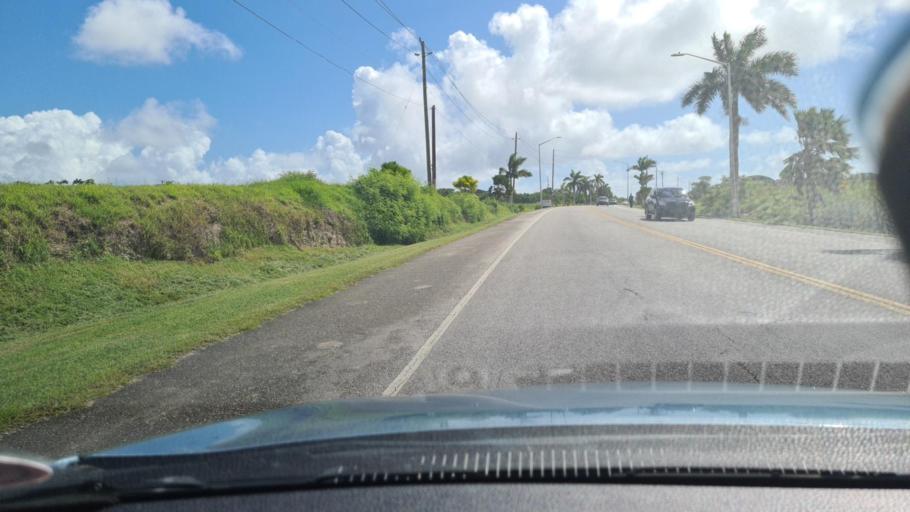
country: BB
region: Christ Church
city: Oistins
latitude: 13.0828
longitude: -59.5347
